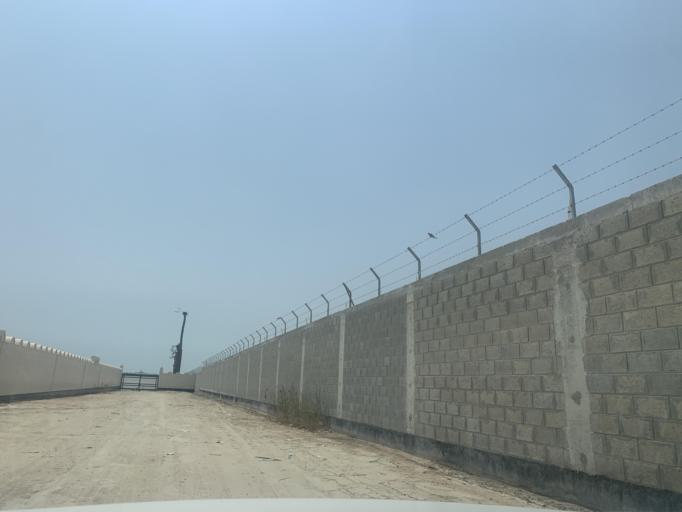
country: BH
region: Central Governorate
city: Madinat Hamad
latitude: 26.1288
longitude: 50.4616
